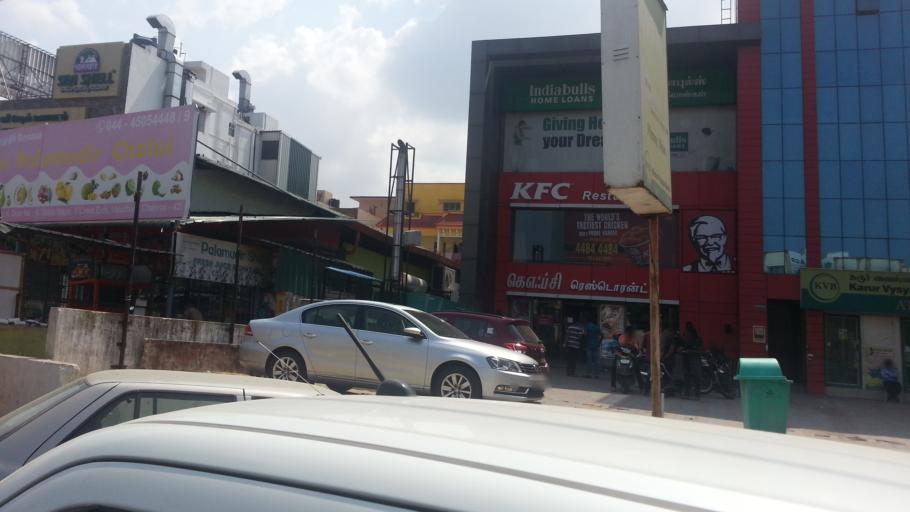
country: IN
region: Tamil Nadu
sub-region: Kancheepuram
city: Madipakkam
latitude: 12.9727
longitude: 80.2195
